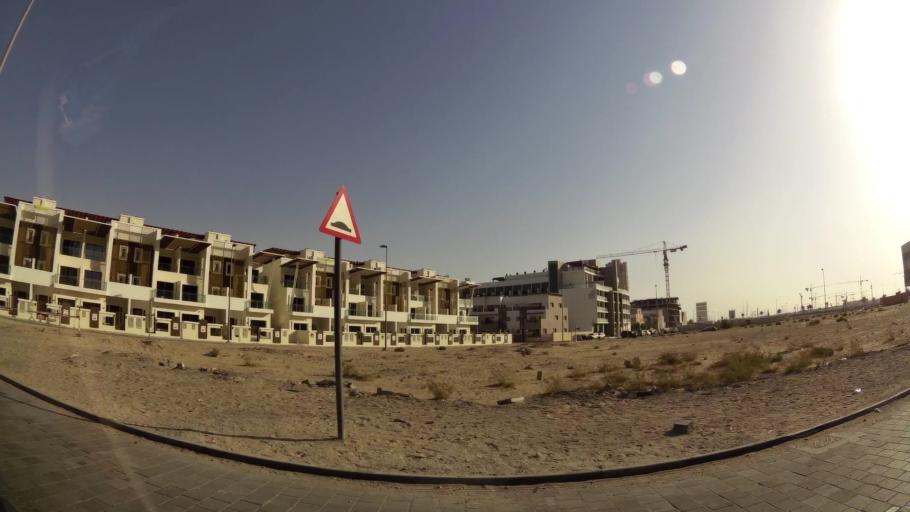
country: AE
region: Dubai
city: Dubai
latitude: 25.0522
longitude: 55.2011
